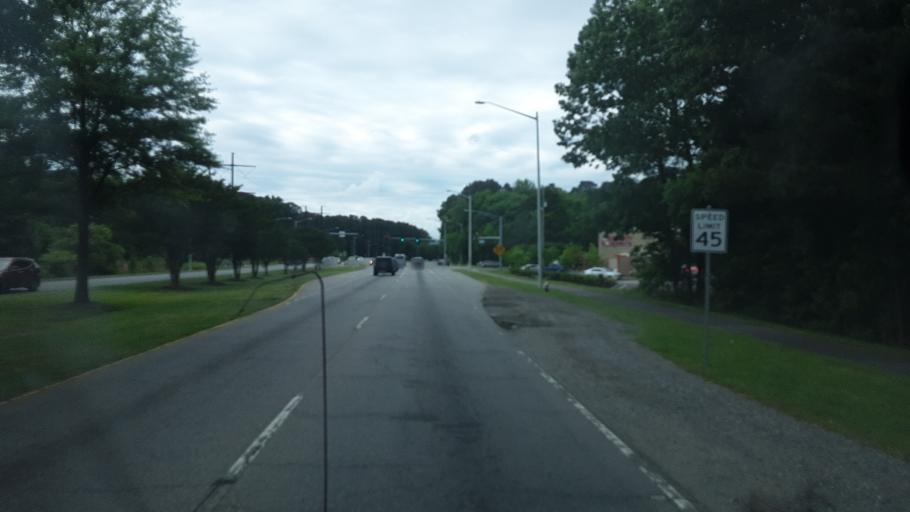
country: US
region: Virginia
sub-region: City of Virginia Beach
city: Virginia Beach
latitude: 36.7952
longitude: -75.9951
